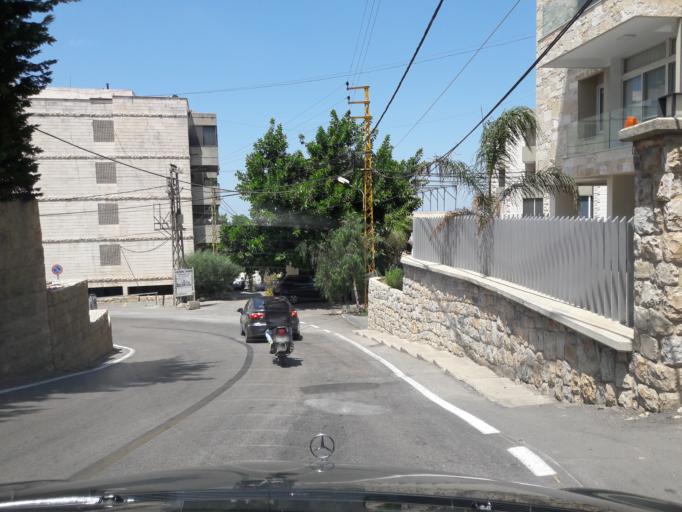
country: LB
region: Mont-Liban
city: Djounie
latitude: 33.9338
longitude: 35.6237
